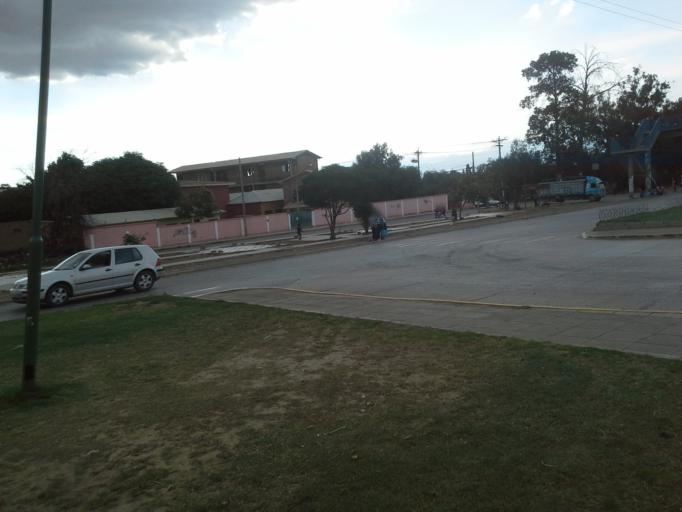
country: BO
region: Cochabamba
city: Cochabamba
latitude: -17.4525
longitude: -66.1284
